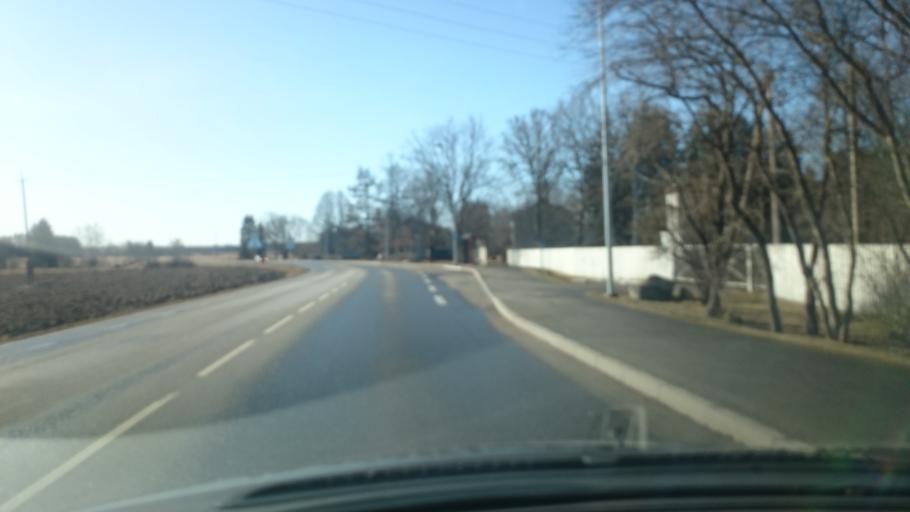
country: EE
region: Harju
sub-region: Saku vald
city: Saku
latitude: 59.2753
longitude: 24.7195
